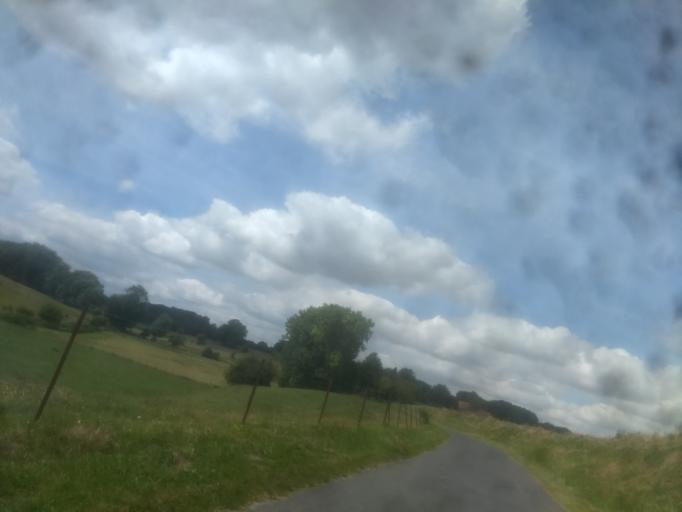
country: FR
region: Nord-Pas-de-Calais
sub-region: Departement du Pas-de-Calais
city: Beaumetz-les-Loges
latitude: 50.2266
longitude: 2.6545
